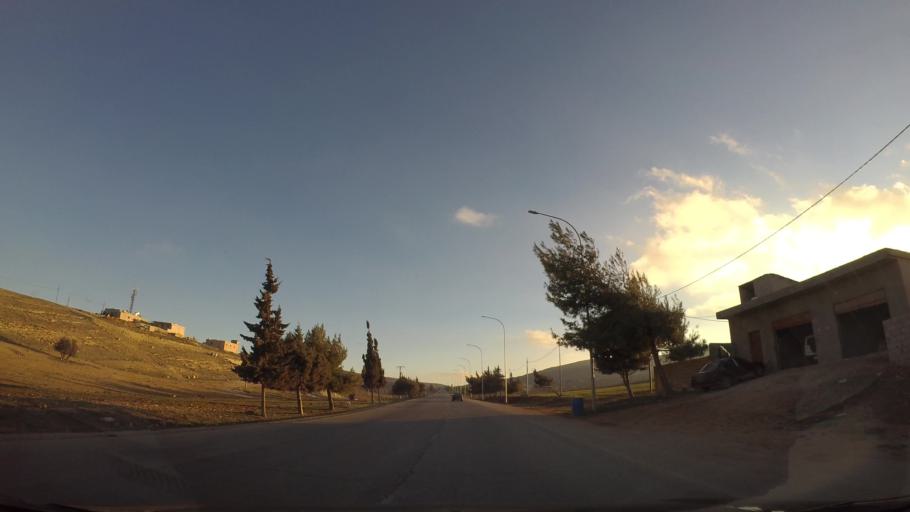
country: JO
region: Ma'an
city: Petra
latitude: 30.4398
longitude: 35.5188
